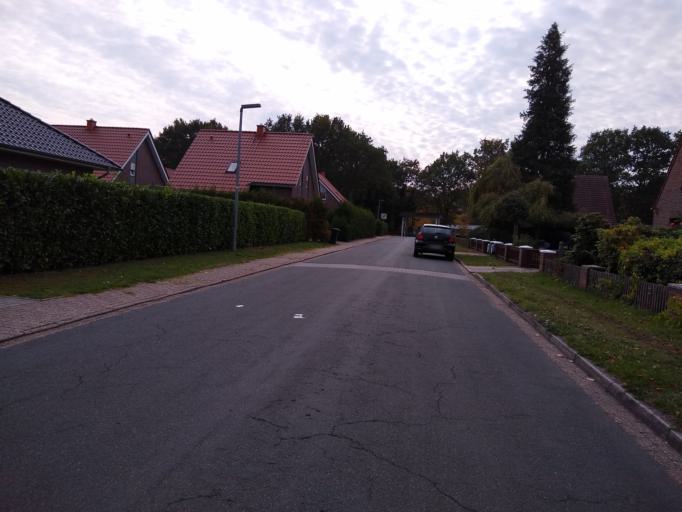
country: DE
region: Lower Saxony
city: Rastede
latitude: 53.2064
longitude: 8.2311
